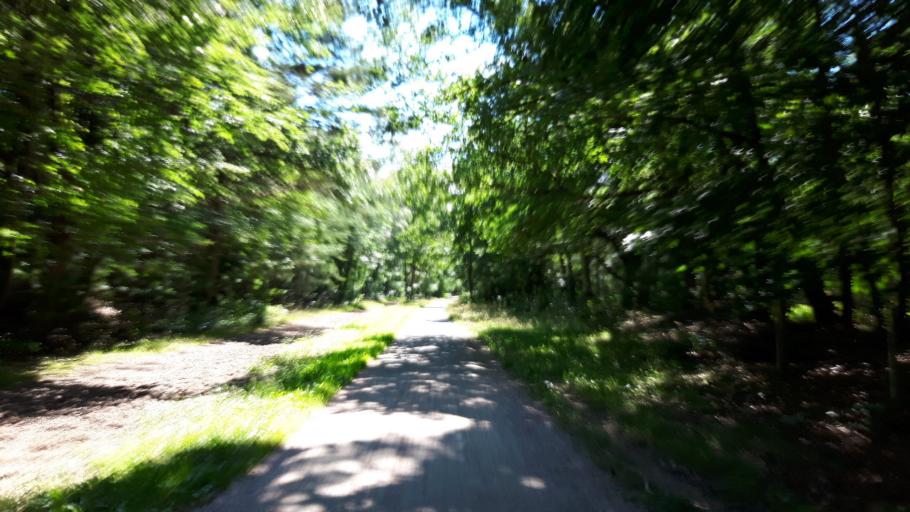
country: NL
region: North Holland
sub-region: Gemeente Wijdemeren
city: Nieuw-Loosdrecht
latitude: 52.2001
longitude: 5.1580
